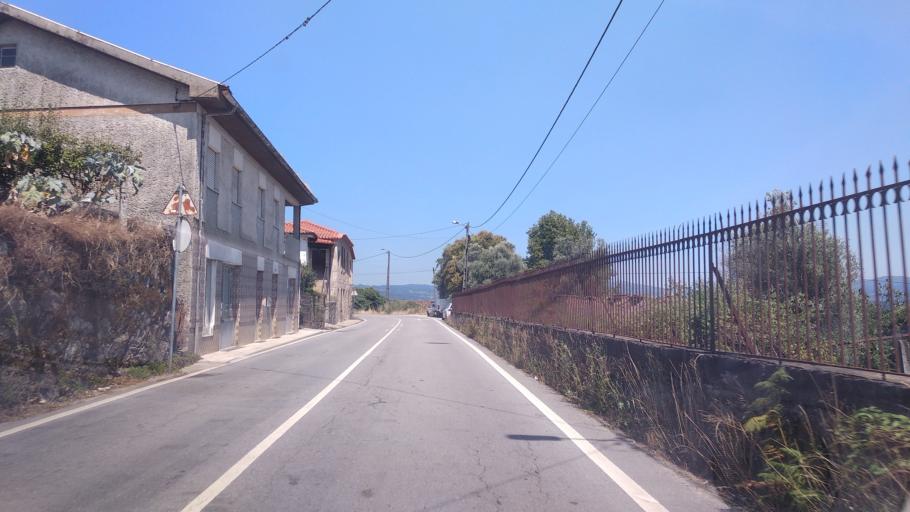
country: PT
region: Braga
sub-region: Braga
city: Adaufe
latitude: 41.5862
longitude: -8.3964
